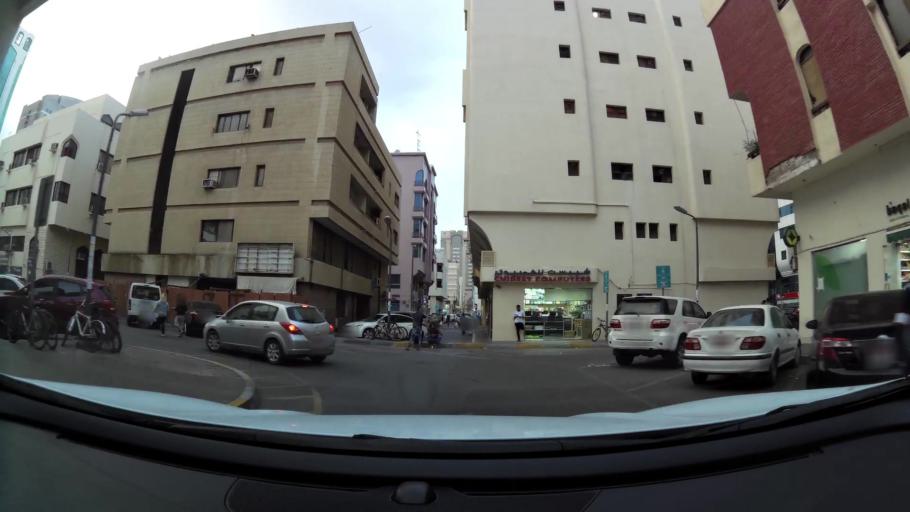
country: AE
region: Abu Dhabi
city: Abu Dhabi
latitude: 24.4926
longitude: 54.3707
